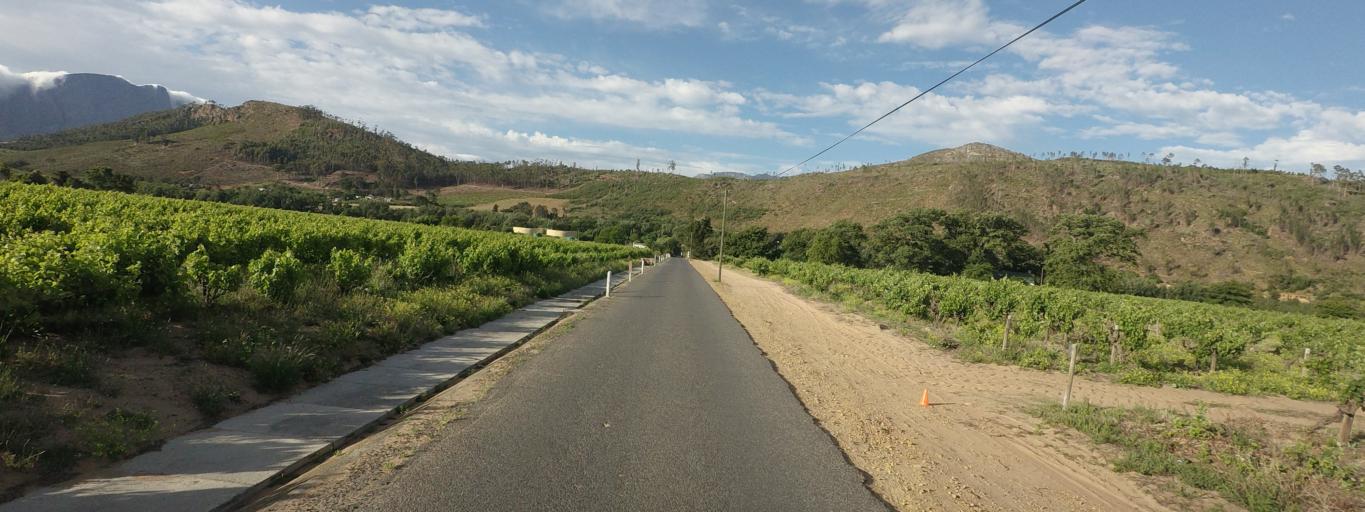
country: ZA
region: Western Cape
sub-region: Cape Winelands District Municipality
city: Paarl
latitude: -33.8957
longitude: 19.0958
